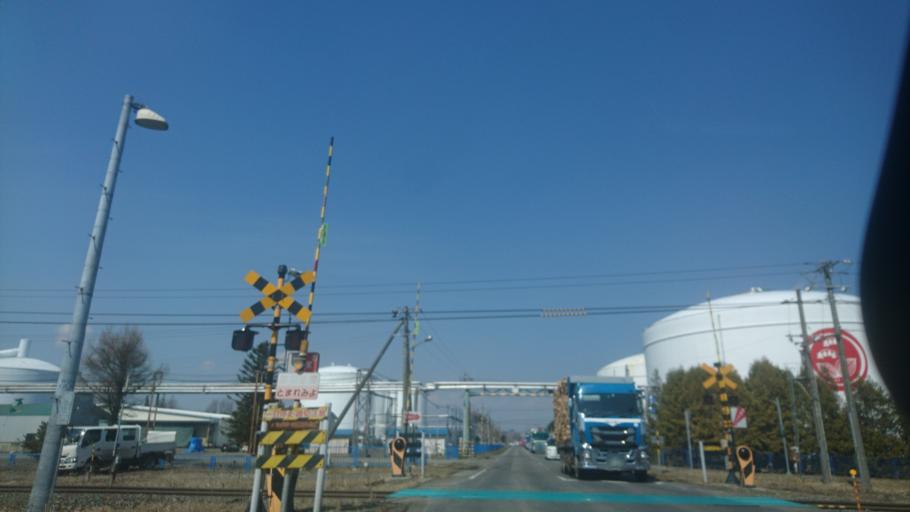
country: JP
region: Hokkaido
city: Obihiro
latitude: 42.9207
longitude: 143.0826
